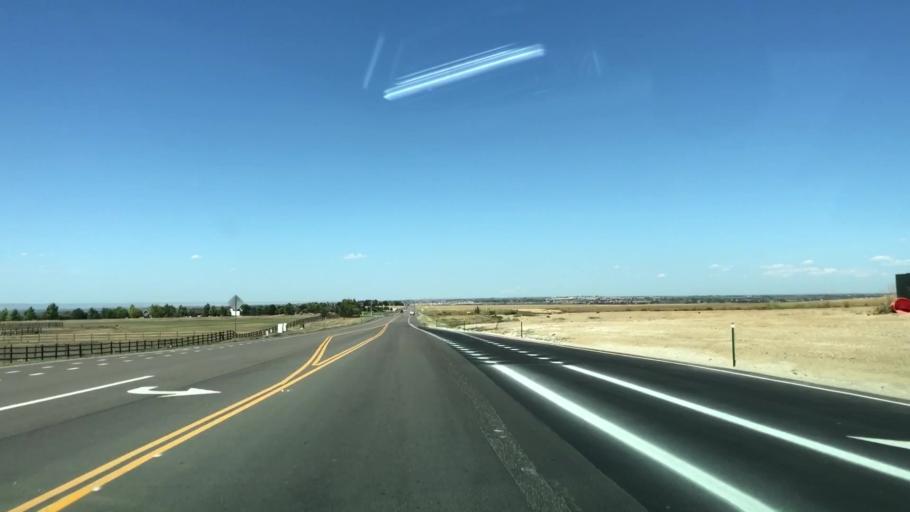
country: US
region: Colorado
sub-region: Weld County
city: Windsor
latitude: 40.4464
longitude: -104.9441
